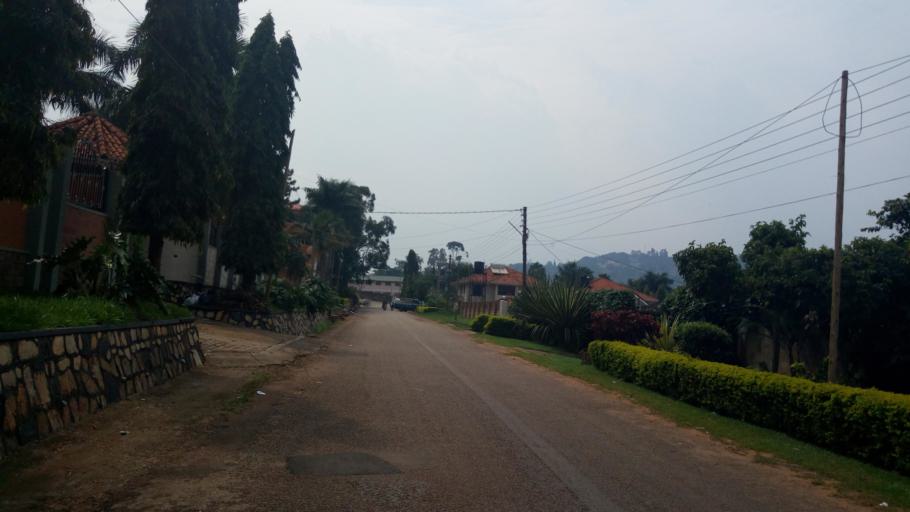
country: UG
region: Central Region
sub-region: Wakiso District
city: Kireka
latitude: 0.3111
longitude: 32.6282
